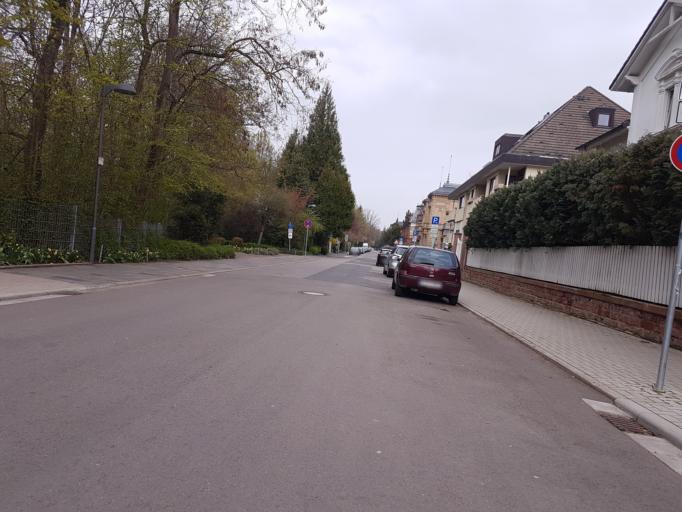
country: DE
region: Rheinland-Pfalz
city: Landau in der Pfalz
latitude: 49.1966
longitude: 8.1075
